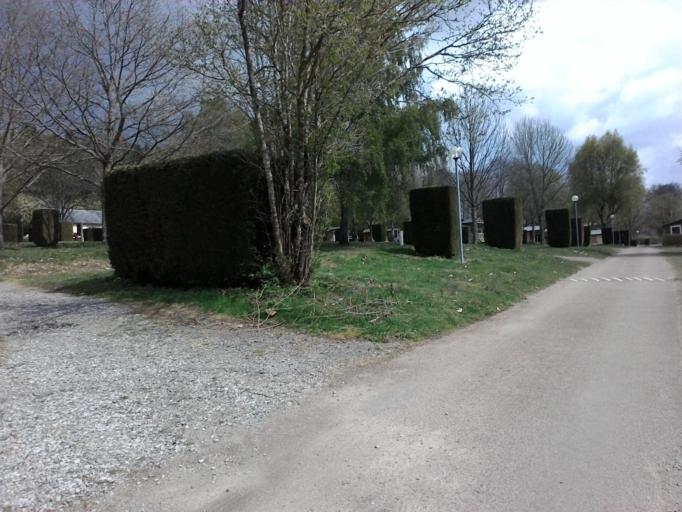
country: FR
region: Bourgogne
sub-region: Departement de la Nievre
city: Chateau-Chinon(Ville)
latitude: 47.1851
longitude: 4.0715
